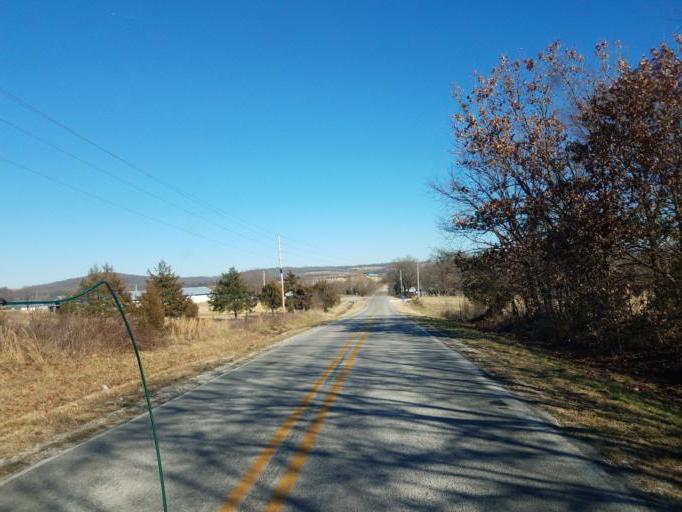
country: US
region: Arkansas
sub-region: Washington County
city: Elkins
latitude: 36.0329
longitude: -93.9745
